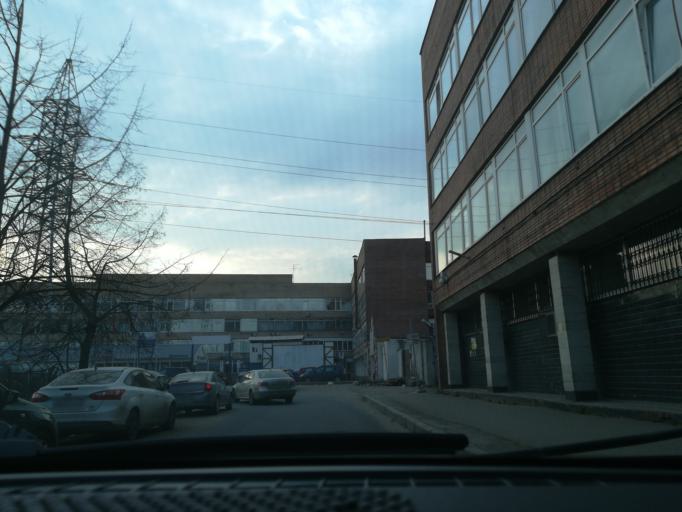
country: RU
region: St.-Petersburg
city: Avtovo
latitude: 59.8786
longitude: 30.2562
